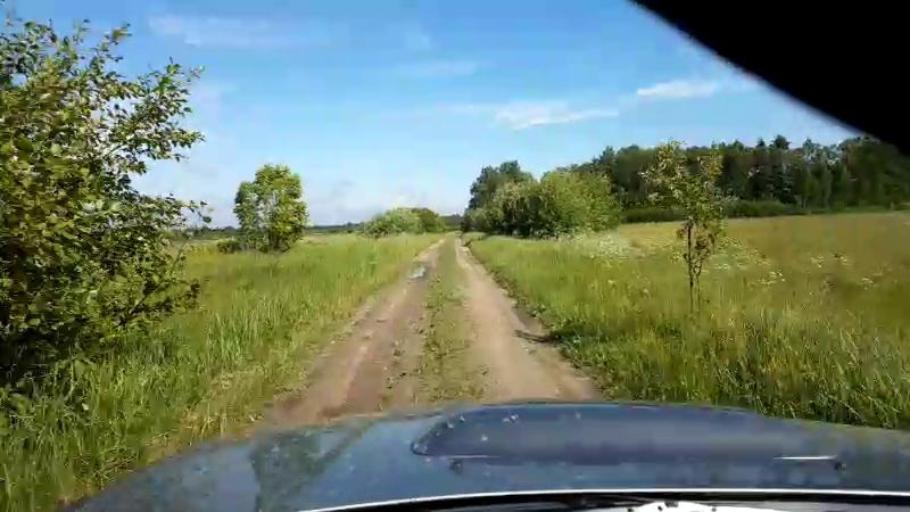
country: EE
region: Paernumaa
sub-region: Sindi linn
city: Sindi
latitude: 58.5015
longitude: 24.7002
